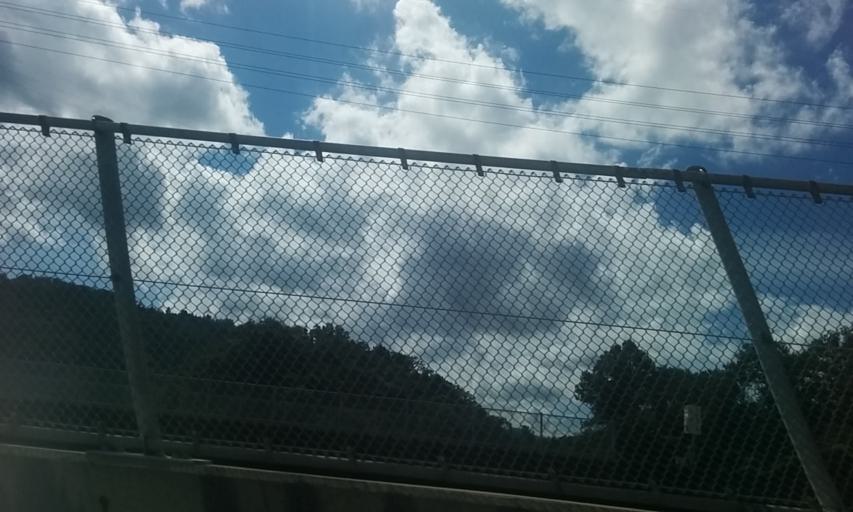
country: JP
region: Kyoto
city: Uji
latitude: 34.9165
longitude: 135.8687
